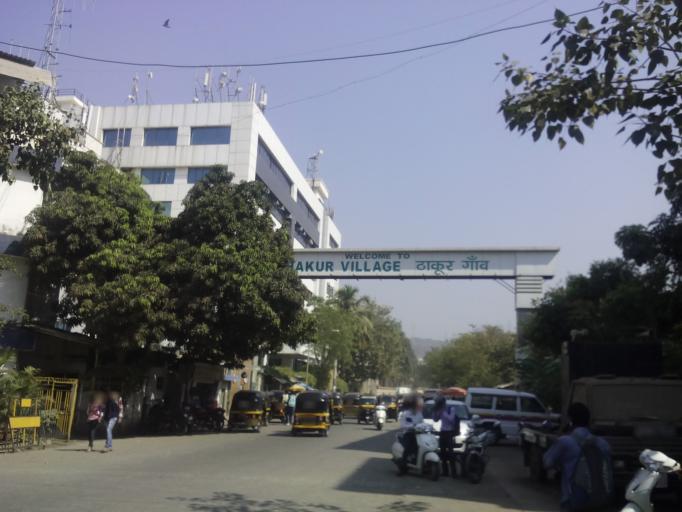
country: IN
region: Maharashtra
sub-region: Mumbai Suburban
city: Borivli
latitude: 19.2054
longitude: 72.8717
